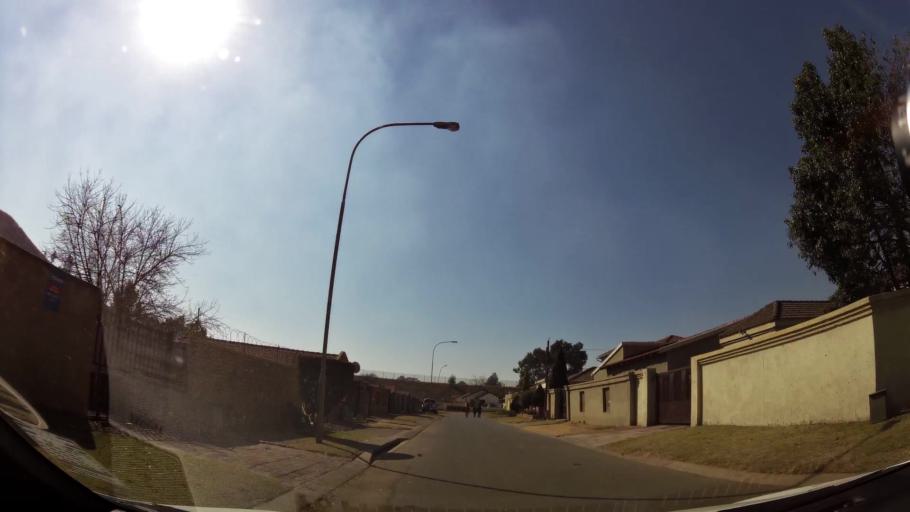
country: ZA
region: Gauteng
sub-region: City of Johannesburg Metropolitan Municipality
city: Johannesburg
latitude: -26.2350
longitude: 28.0651
